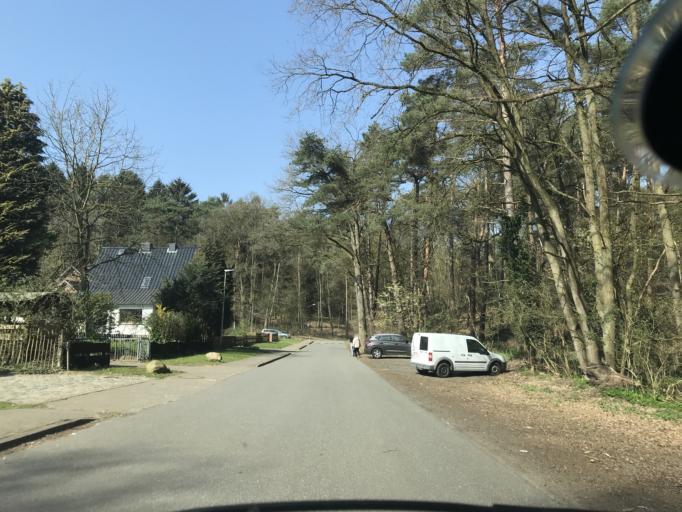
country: DE
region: Lower Saxony
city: Buxtehude
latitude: 53.4509
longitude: 9.7299
